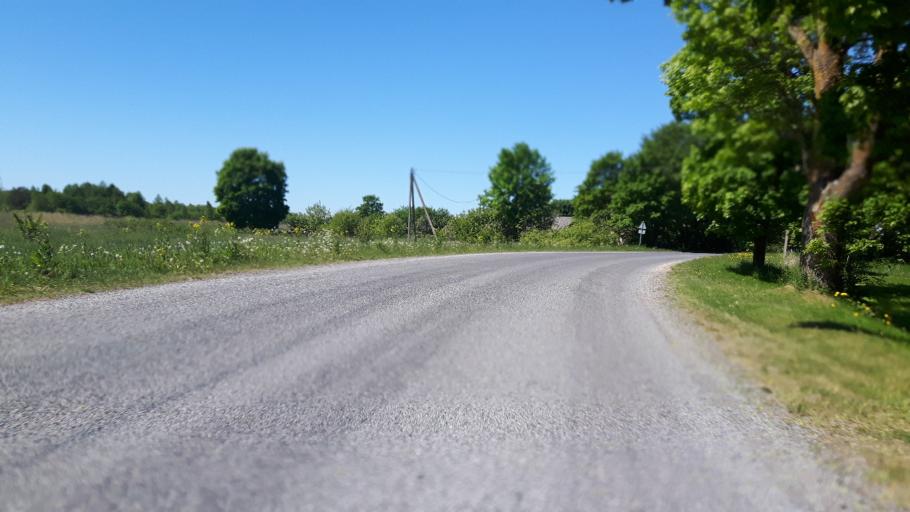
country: EE
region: Ida-Virumaa
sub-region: Sillamaee linn
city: Sillamae
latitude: 59.3828
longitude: 27.8154
